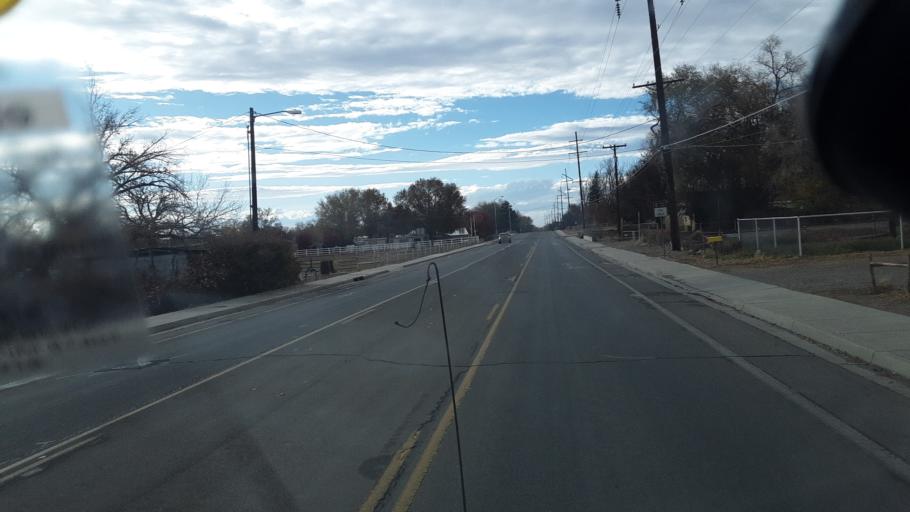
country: US
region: New Mexico
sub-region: San Juan County
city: Farmington
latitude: 36.7265
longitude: -108.1782
